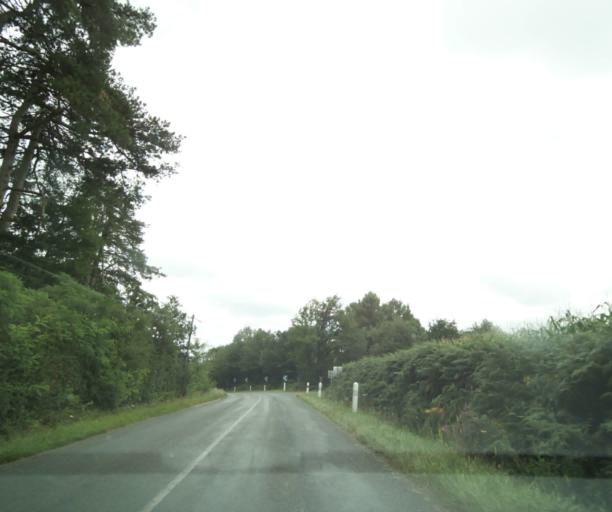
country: FR
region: Pays de la Loire
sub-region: Departement de Maine-et-Loire
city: Durtal
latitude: 47.7053
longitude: -0.2689
